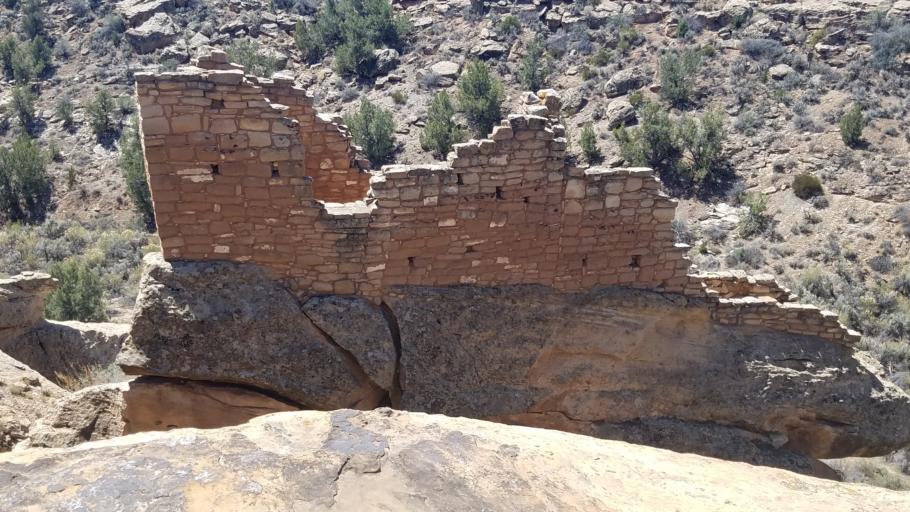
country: US
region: Colorado
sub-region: Montezuma County
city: Towaoc
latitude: 37.3835
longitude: -109.0757
